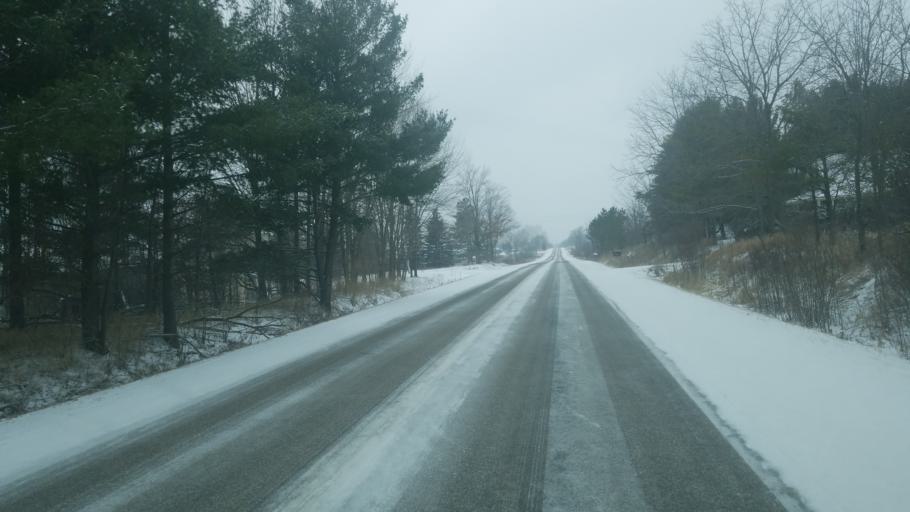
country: US
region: Michigan
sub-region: Osceola County
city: Evart
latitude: 44.1025
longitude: -85.1771
